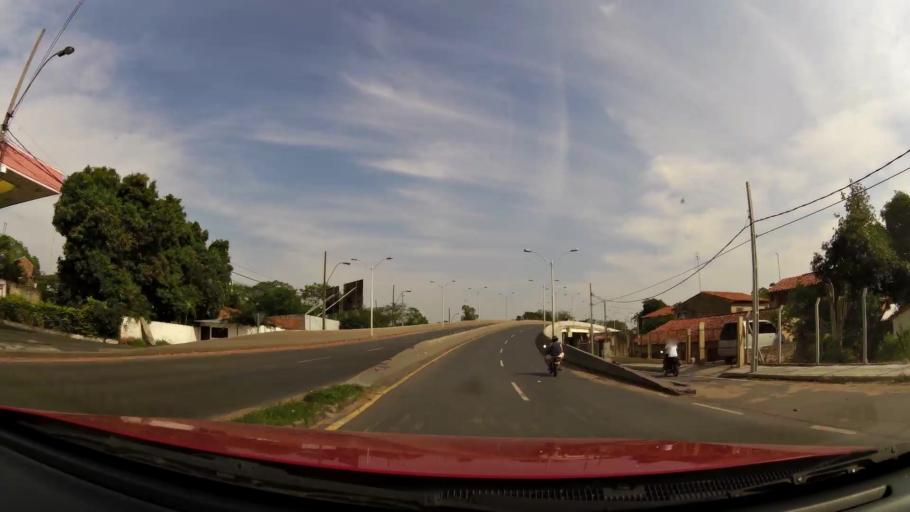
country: PY
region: Central
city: Fernando de la Mora
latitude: -25.2576
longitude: -57.5509
